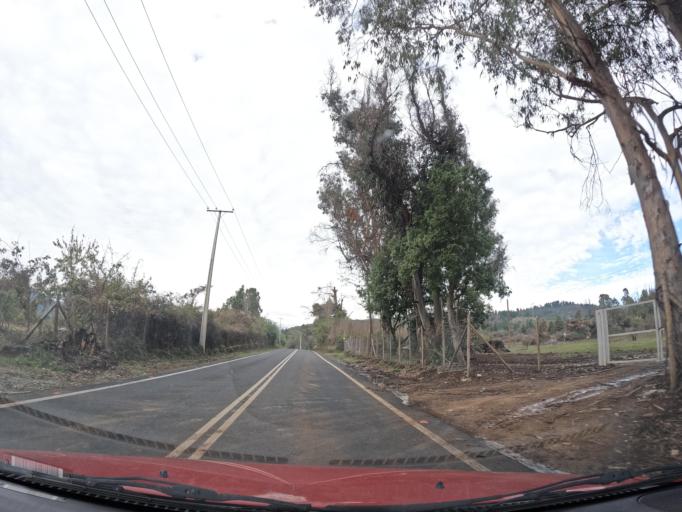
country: CL
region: Maule
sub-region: Provincia de Linares
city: Linares
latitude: -35.9176
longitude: -71.4633
